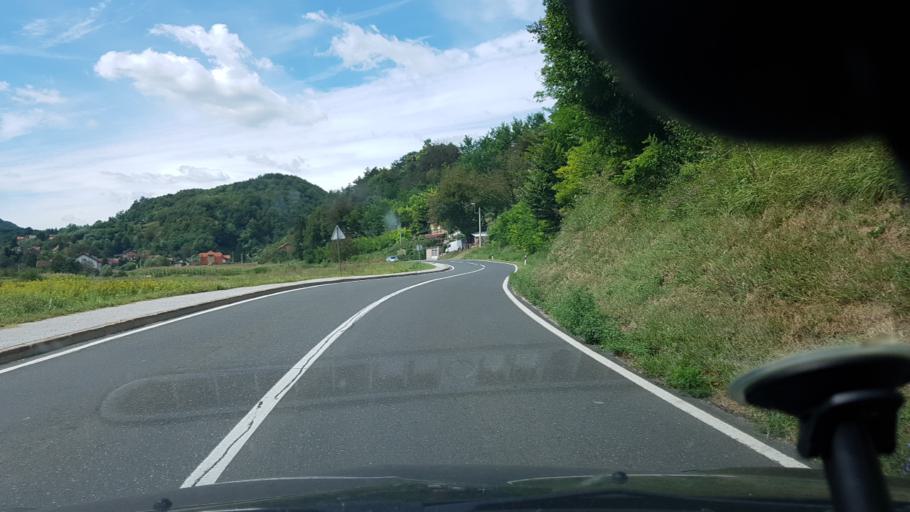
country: HR
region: Varazdinska
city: Lepoglava
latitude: 46.2069
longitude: 16.0277
